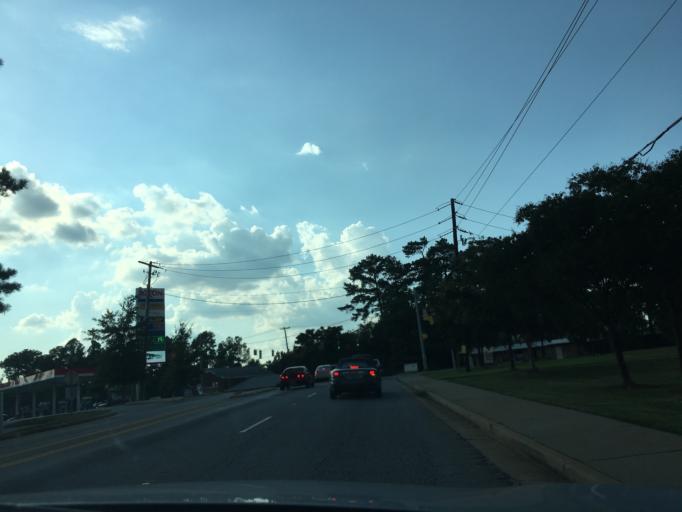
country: US
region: South Carolina
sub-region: Richland County
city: Lake Murray of Richland
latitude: 34.1244
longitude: -81.2332
